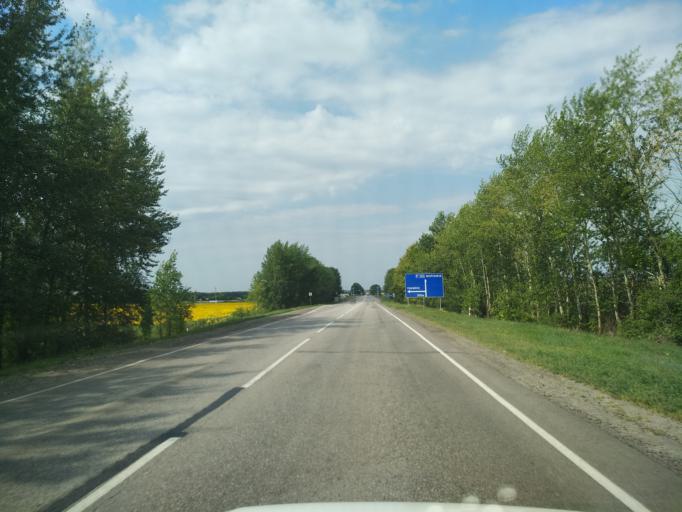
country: RU
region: Voronezj
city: Verkhnyaya Khava
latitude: 51.6907
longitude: 39.9364
